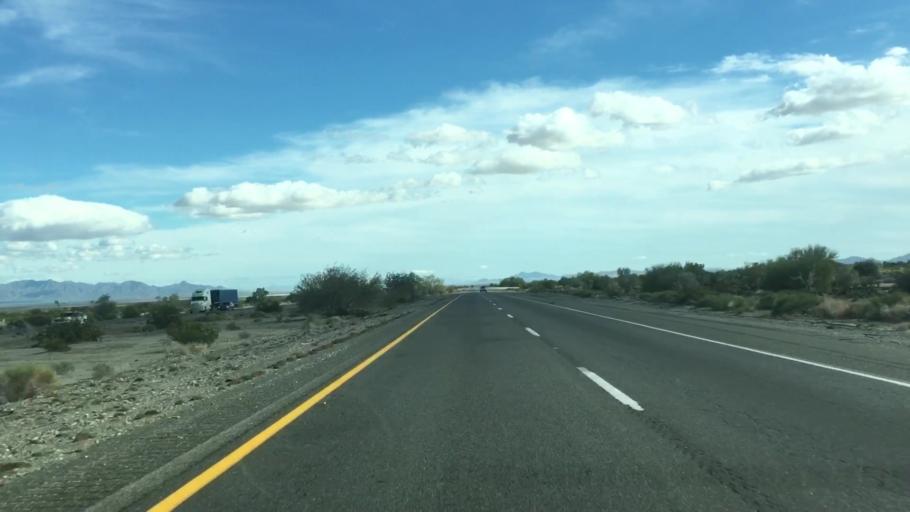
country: US
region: California
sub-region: Riverside County
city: Mesa Verde
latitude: 33.6593
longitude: -115.1658
